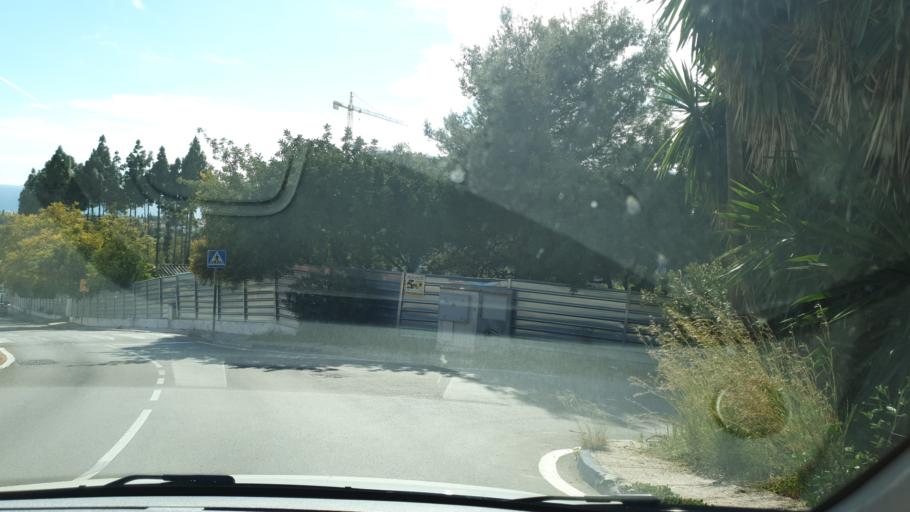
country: ES
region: Andalusia
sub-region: Provincia de Malaga
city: Marbella
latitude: 36.5274
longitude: -4.8898
